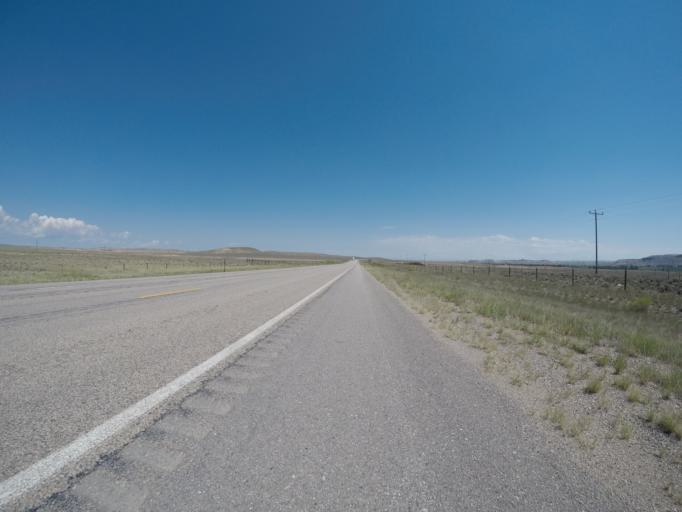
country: US
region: Wyoming
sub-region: Sublette County
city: Marbleton
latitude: 42.4215
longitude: -110.1118
